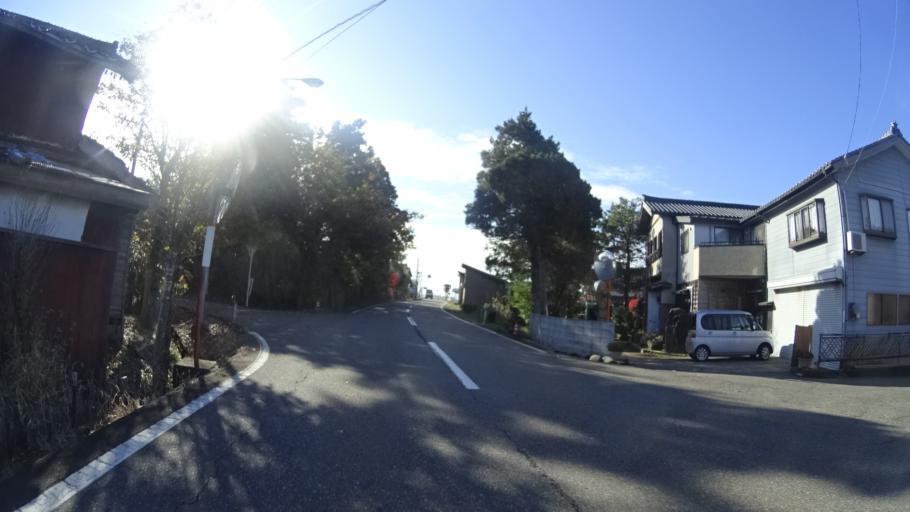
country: JP
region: Niigata
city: Mitsuke
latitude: 37.5581
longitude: 138.8492
